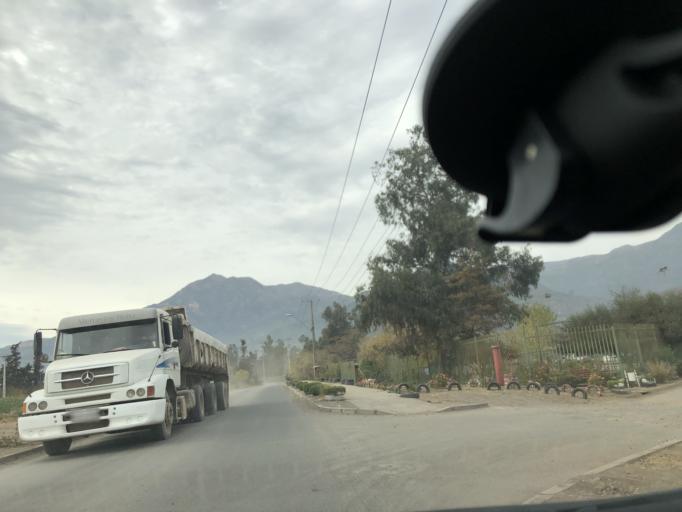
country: CL
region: Santiago Metropolitan
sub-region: Provincia de Cordillera
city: Puente Alto
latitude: -33.6060
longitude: -70.5169
